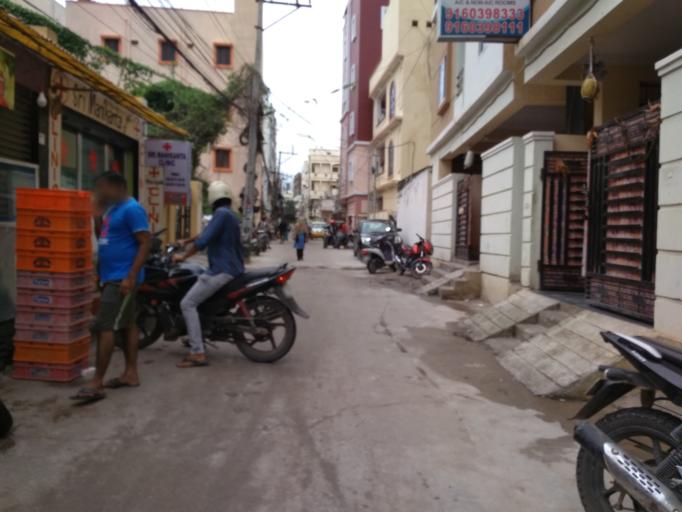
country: IN
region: Telangana
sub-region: Rangareddi
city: Kukatpalli
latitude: 17.4425
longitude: 78.3604
